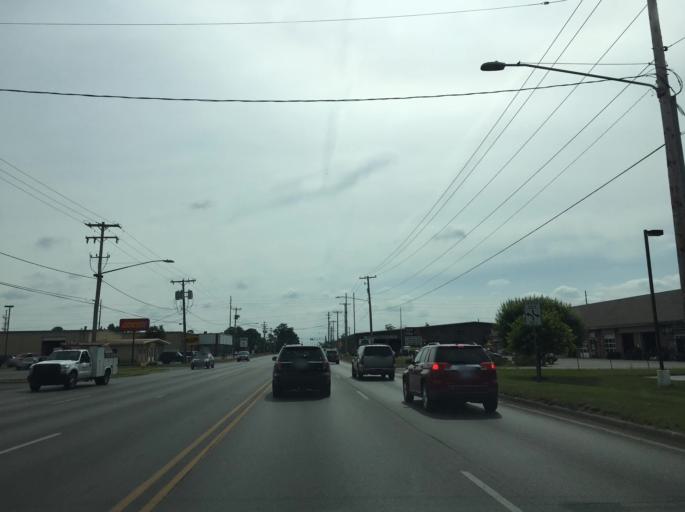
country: US
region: Michigan
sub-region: Grand Traverse County
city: Traverse City
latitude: 44.7336
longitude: -85.6249
